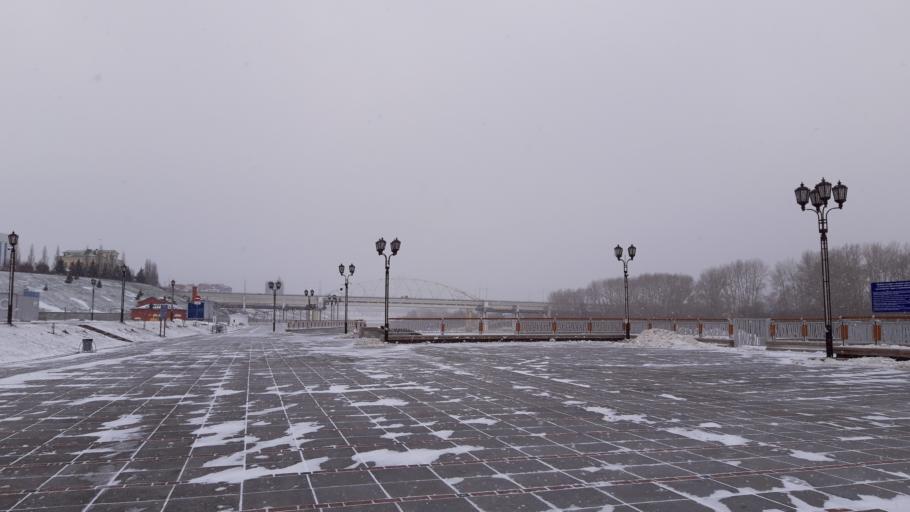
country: RU
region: Tjumen
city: Tyumen
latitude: 57.1621
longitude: 65.5488
